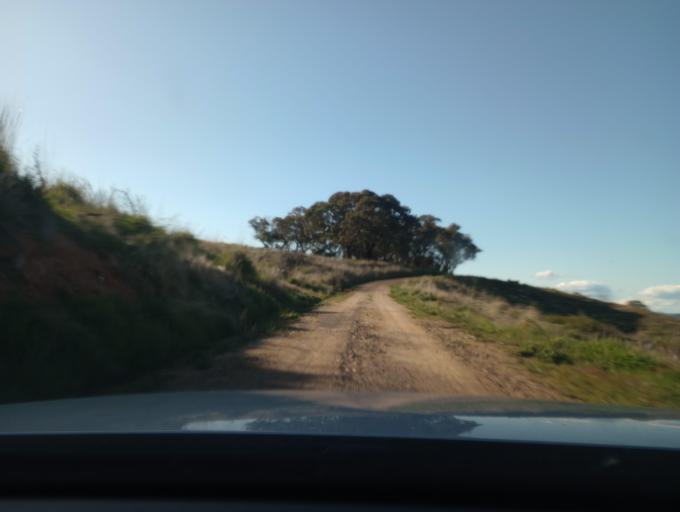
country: AU
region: New South Wales
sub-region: Blayney
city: Blayney
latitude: -33.4202
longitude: 149.3138
